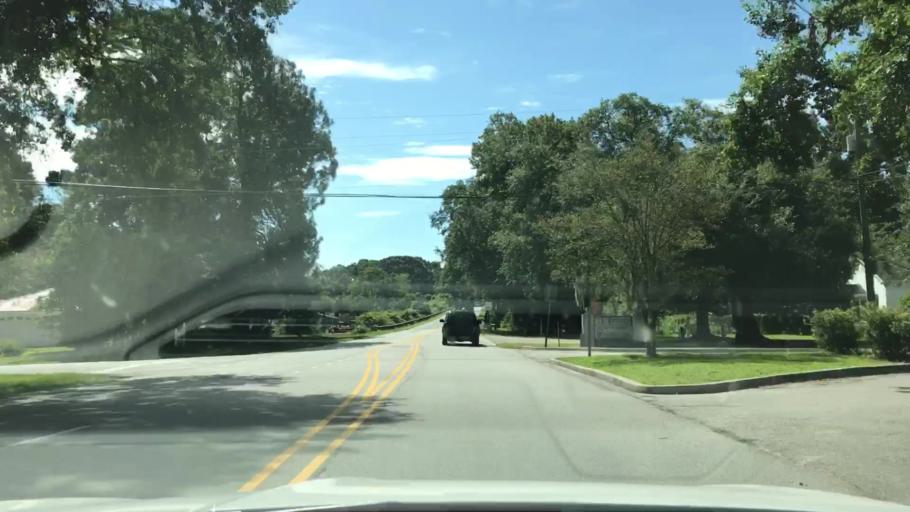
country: US
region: South Carolina
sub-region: Charleston County
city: Shell Point
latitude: 32.8438
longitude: -80.0585
